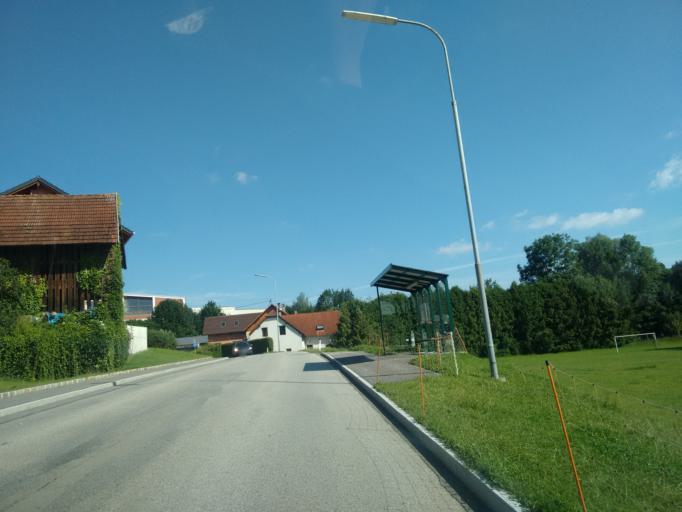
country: AT
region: Upper Austria
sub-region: Politischer Bezirk Steyr-Land
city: Pfarrkirchen bei Bad Hall
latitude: 48.0237
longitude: 14.2069
